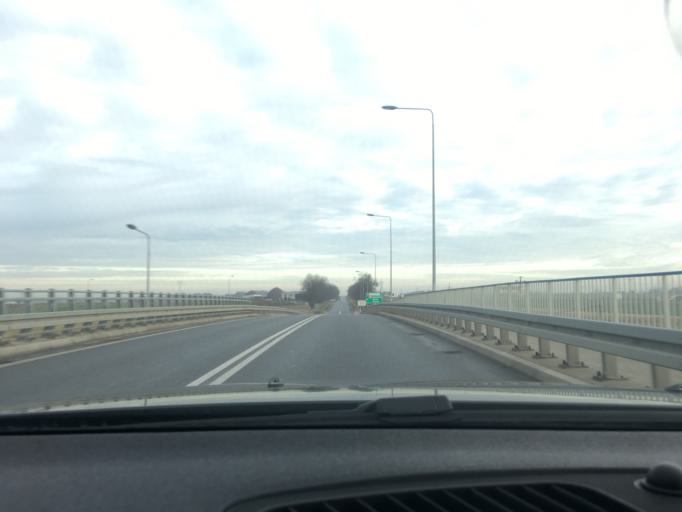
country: PL
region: Swietokrzyskie
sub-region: Powiat jedrzejowski
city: Jedrzejow
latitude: 50.6479
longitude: 20.3156
